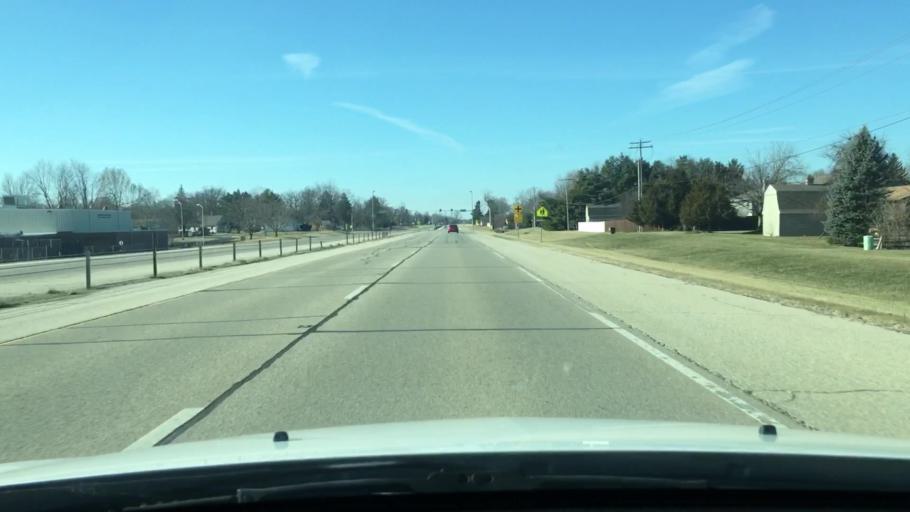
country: US
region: Illinois
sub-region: Woodford County
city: Germantown Hills
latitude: 40.7702
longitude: -89.4491
